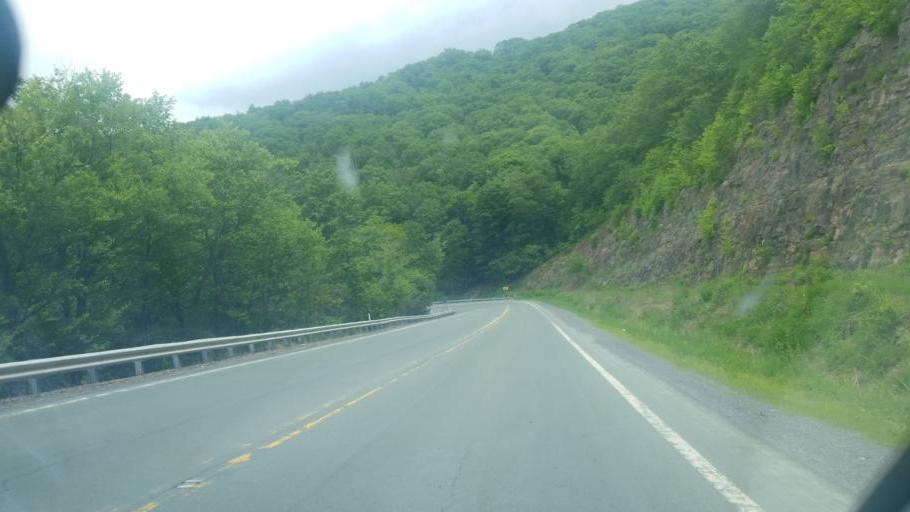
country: US
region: West Virginia
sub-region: Pendleton County
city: Franklin
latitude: 38.5868
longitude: -79.1689
